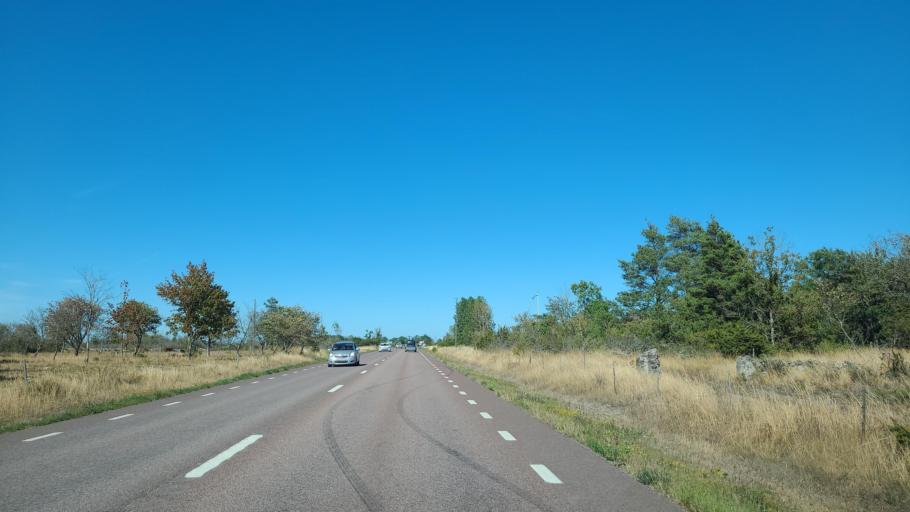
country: SE
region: Kalmar
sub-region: Borgholms Kommun
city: Borgholm
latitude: 57.1130
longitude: 16.9533
